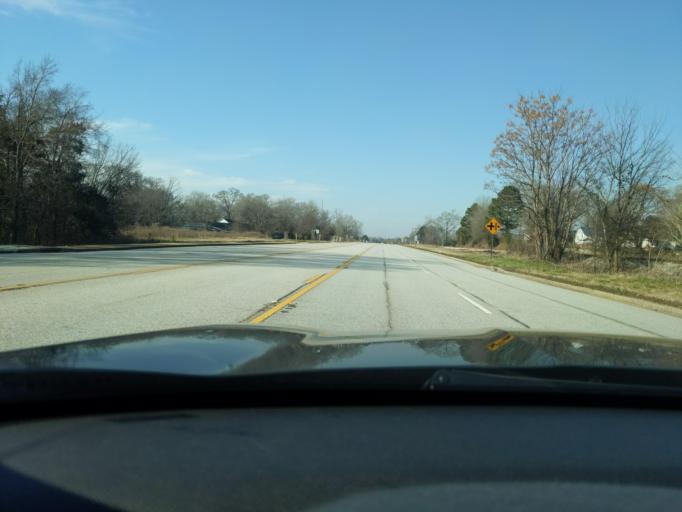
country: US
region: South Carolina
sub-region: Abbeville County
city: Calhoun Falls
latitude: 34.0965
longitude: -82.5837
